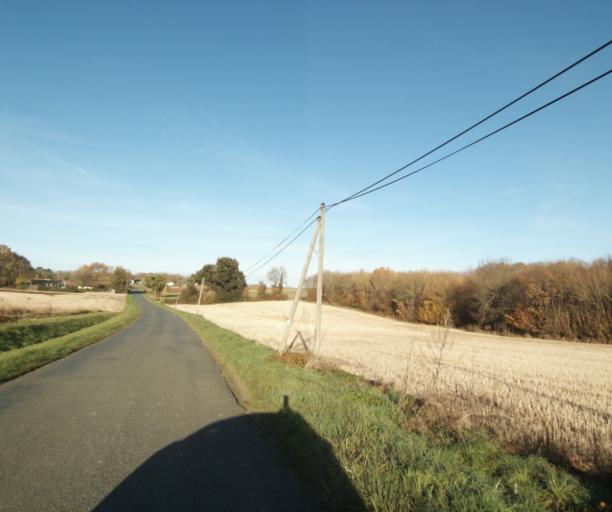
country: FR
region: Poitou-Charentes
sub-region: Departement de la Charente-Maritime
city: Cherac
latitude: 45.7067
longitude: -0.4448
